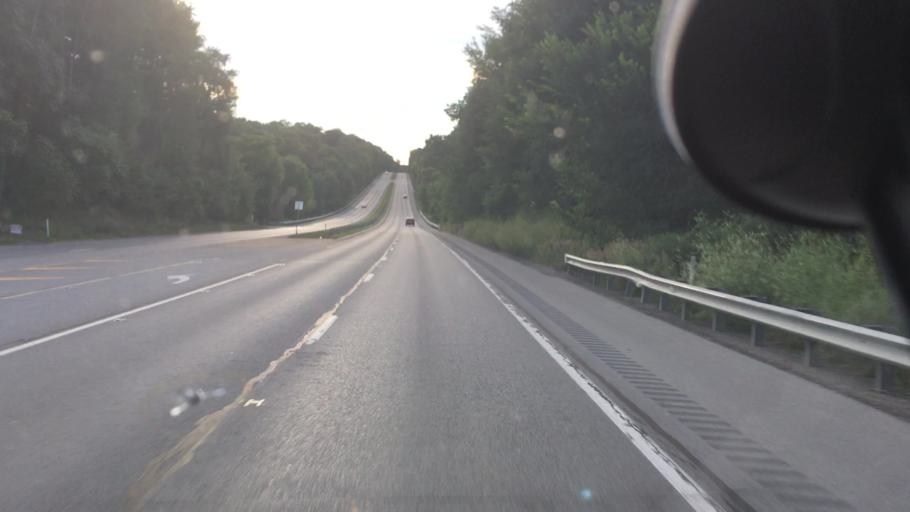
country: US
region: Pennsylvania
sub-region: Beaver County
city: Big Beaver
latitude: 40.7932
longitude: -80.4162
